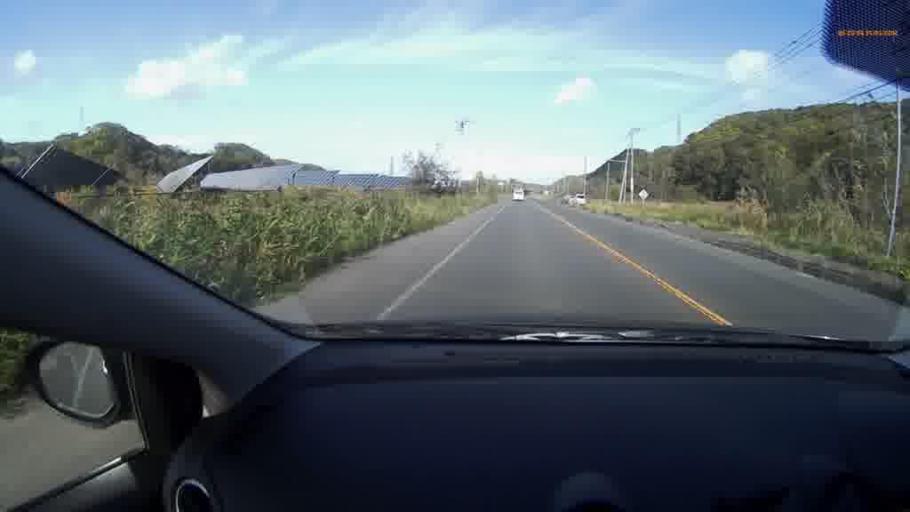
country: JP
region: Hokkaido
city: Kushiro
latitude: 42.9904
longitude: 144.4543
